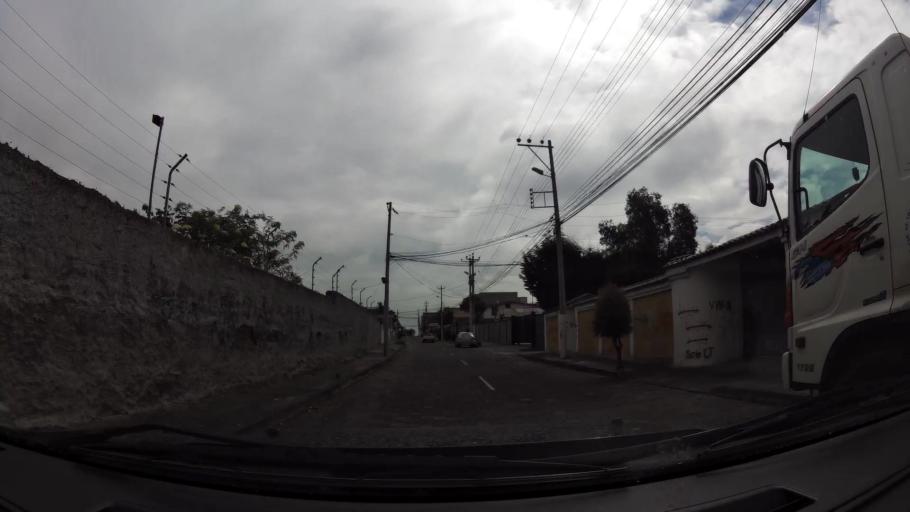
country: EC
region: Pichincha
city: Sangolqui
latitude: -0.2976
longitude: -78.4781
